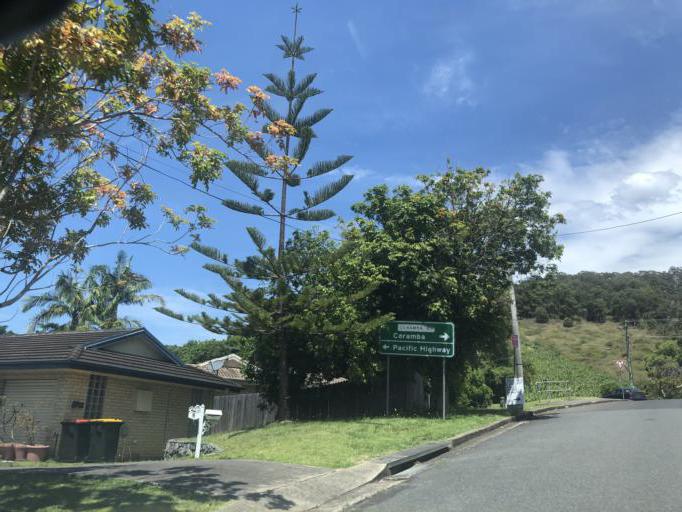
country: AU
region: New South Wales
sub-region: Coffs Harbour
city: Coffs Harbour
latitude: -30.2905
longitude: 153.0970
